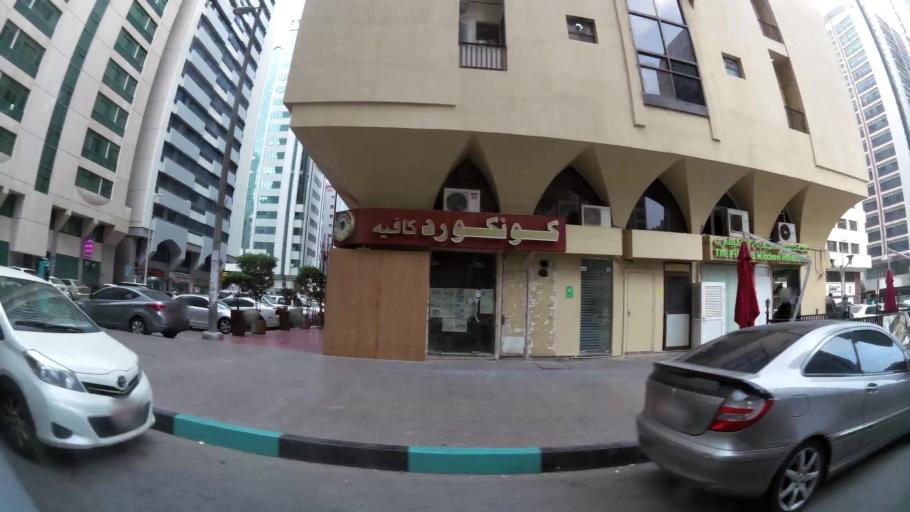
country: AE
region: Abu Dhabi
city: Abu Dhabi
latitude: 24.4939
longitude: 54.3778
